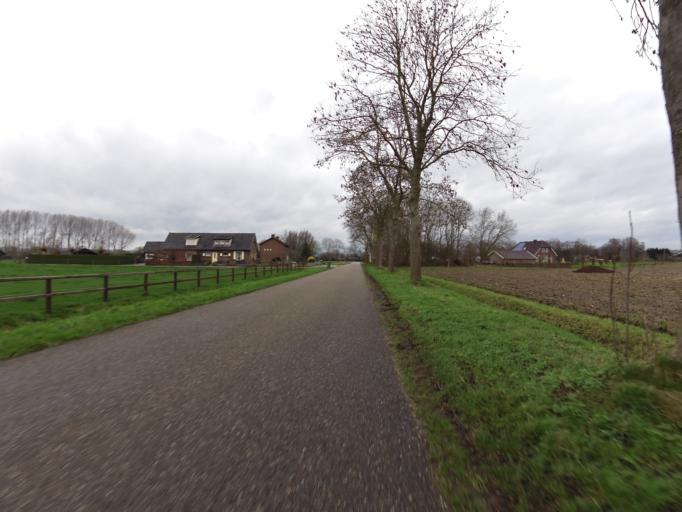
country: NL
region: Gelderland
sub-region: Gemeente Zevenaar
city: Zevenaar
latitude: 51.9223
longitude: 6.1380
